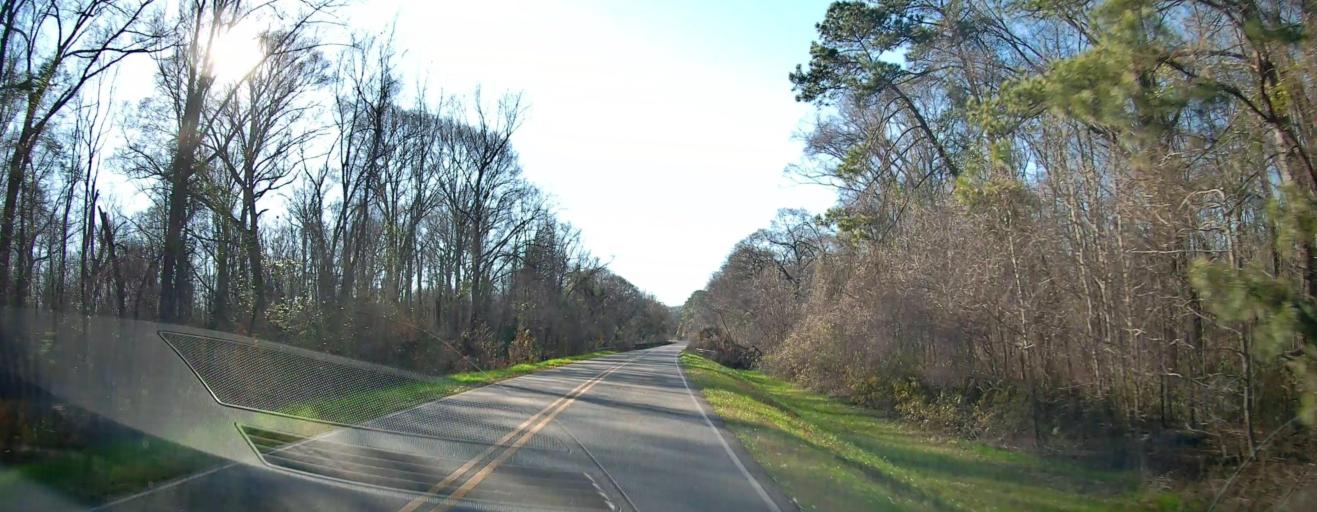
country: US
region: Georgia
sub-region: Sumter County
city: Americus
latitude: 32.0066
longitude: -84.2247
